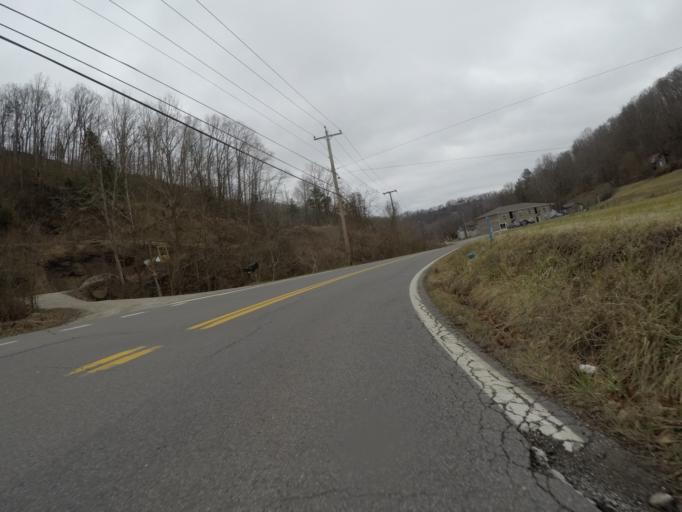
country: US
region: West Virginia
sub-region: Cabell County
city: Barboursville
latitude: 38.4384
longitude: -82.2917
